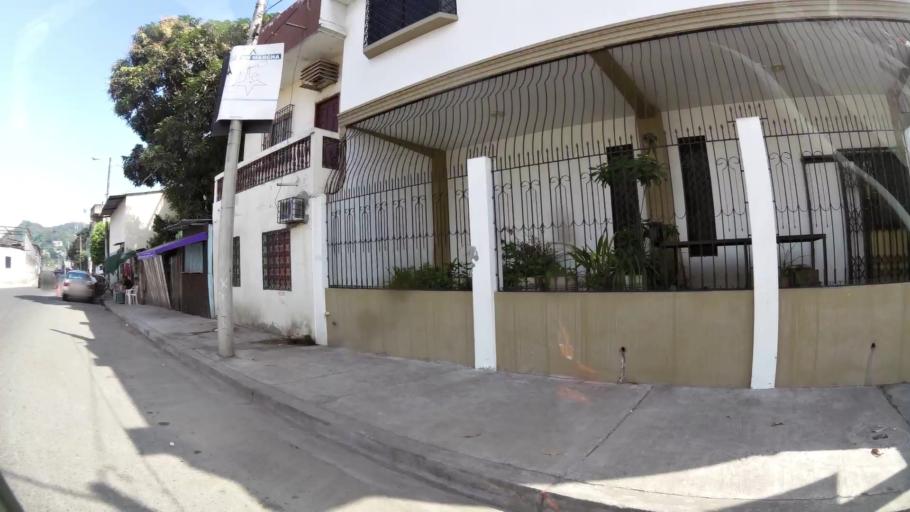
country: EC
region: Guayas
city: Guayaquil
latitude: -2.1530
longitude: -79.9338
